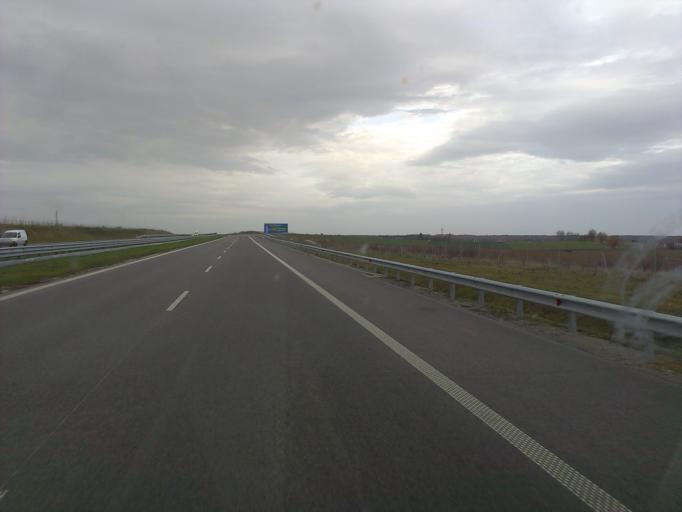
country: PL
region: Subcarpathian Voivodeship
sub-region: Powiat jaroslawski
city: Pawlosiow
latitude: 49.9557
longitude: 22.6611
